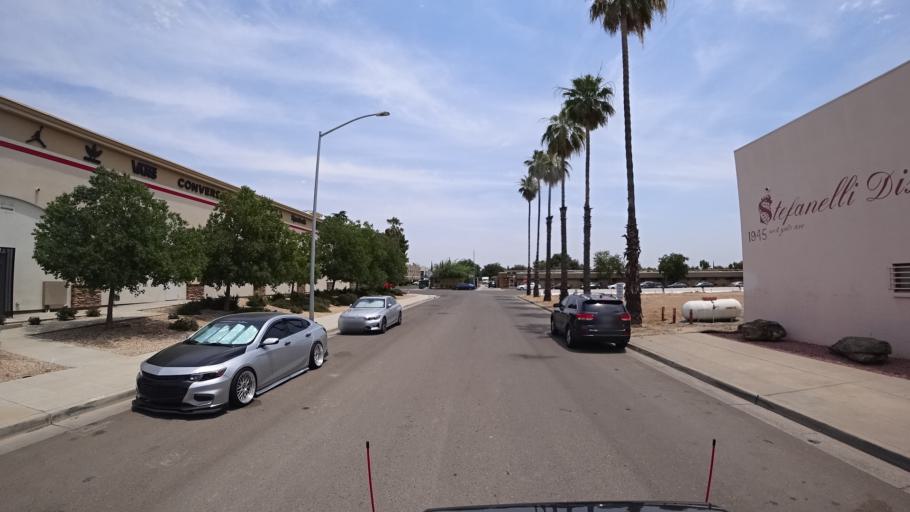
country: US
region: California
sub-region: Fresno County
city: West Park
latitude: 36.7702
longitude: -119.8341
